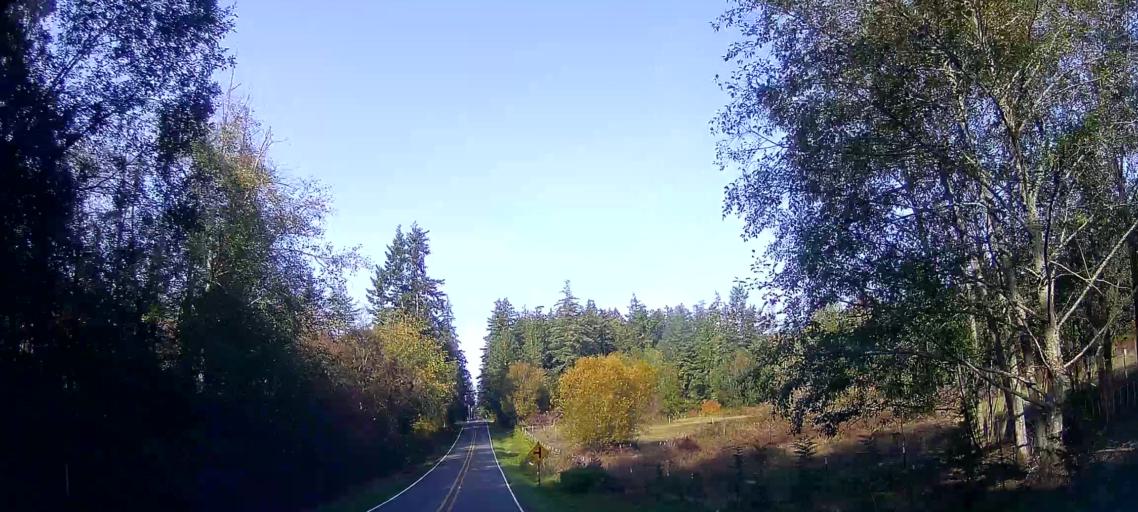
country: US
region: Washington
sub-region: Island County
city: Camano
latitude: 48.2151
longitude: -122.4561
